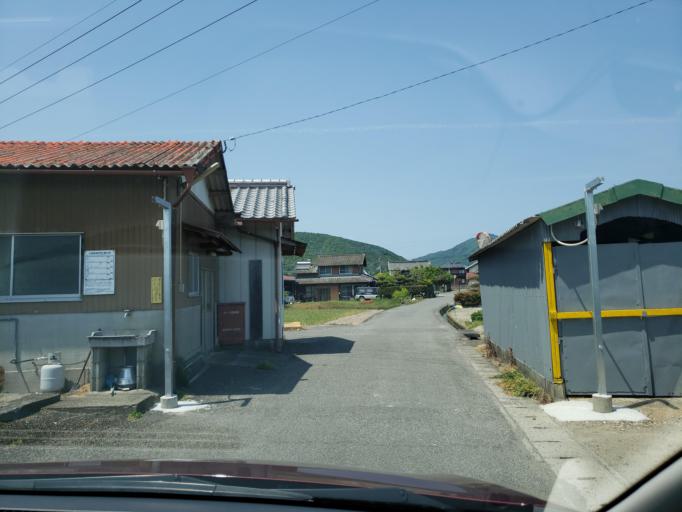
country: JP
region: Tokushima
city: Kamojimacho-jogejima
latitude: 34.0946
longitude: 134.2682
